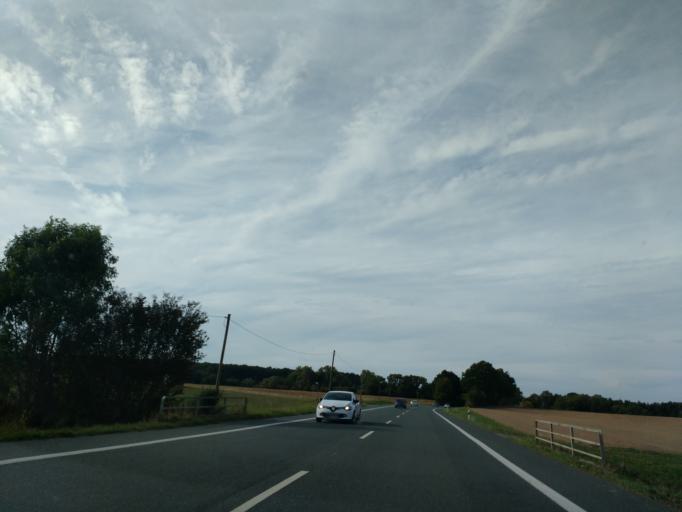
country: DE
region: North Rhine-Westphalia
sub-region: Regierungsbezirk Detmold
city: Nieheim
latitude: 51.8186
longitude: 9.0936
